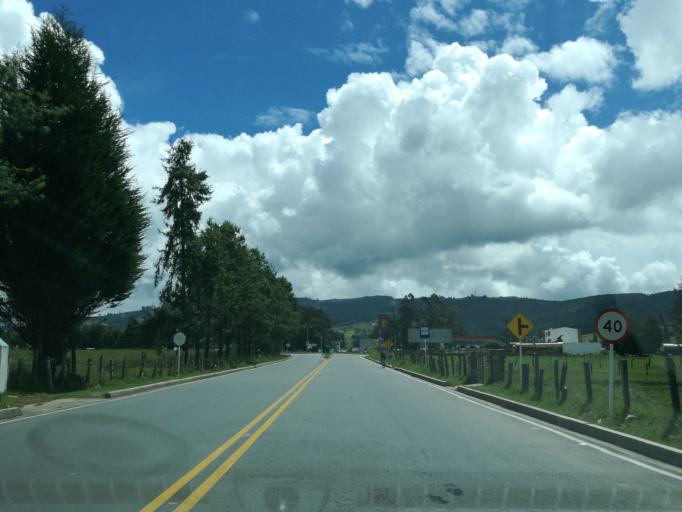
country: CO
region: Boyaca
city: Santa Rosa de Viterbo
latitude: 5.8665
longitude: -72.9919
